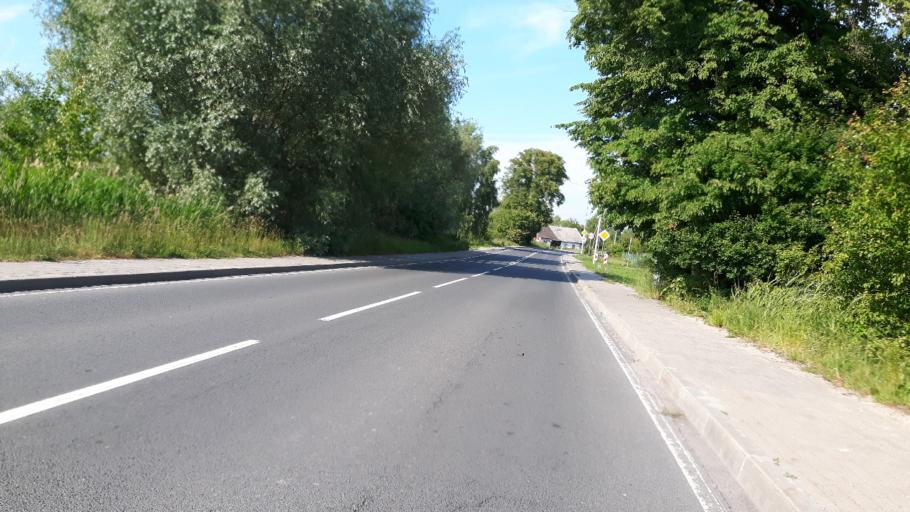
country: RU
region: Kaliningrad
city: Mamonovo
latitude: 54.4592
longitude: 19.9281
